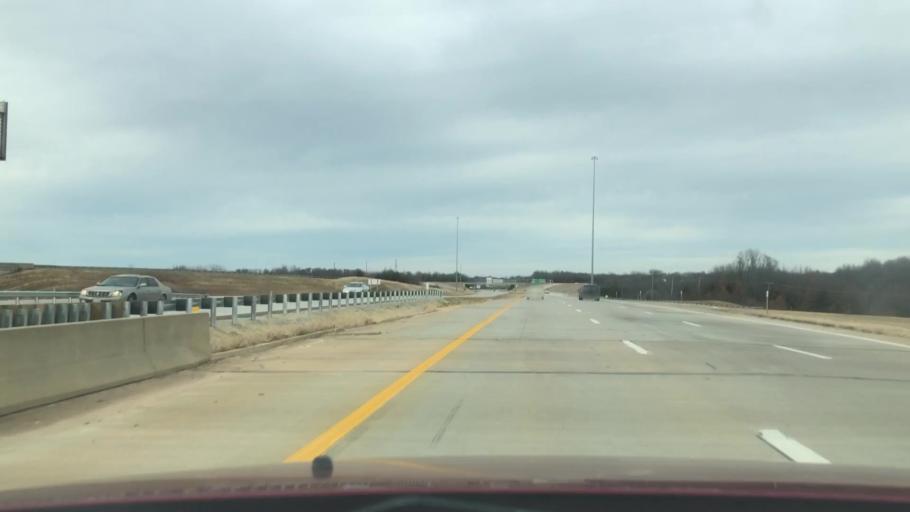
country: US
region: Missouri
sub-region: Greene County
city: Springfield
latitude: 37.2504
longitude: -93.2244
